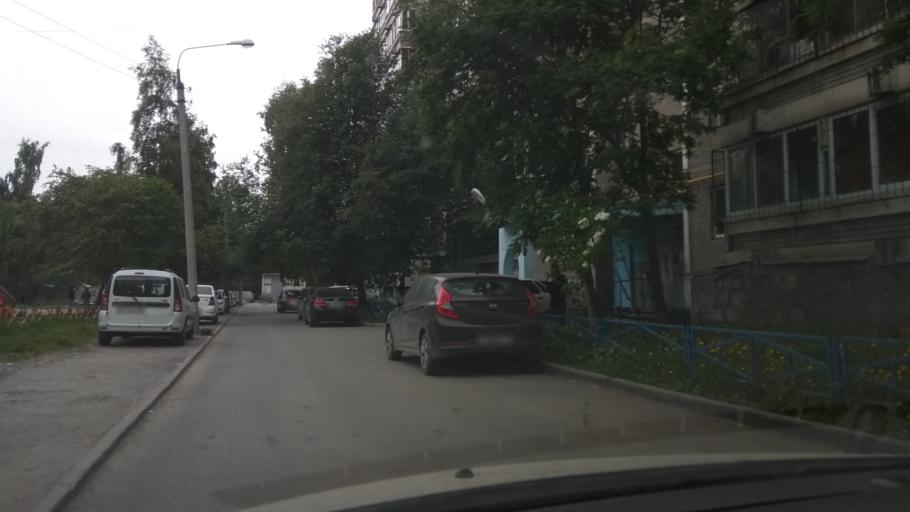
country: RU
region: Sverdlovsk
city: Sovkhoznyy
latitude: 56.7981
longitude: 60.5827
